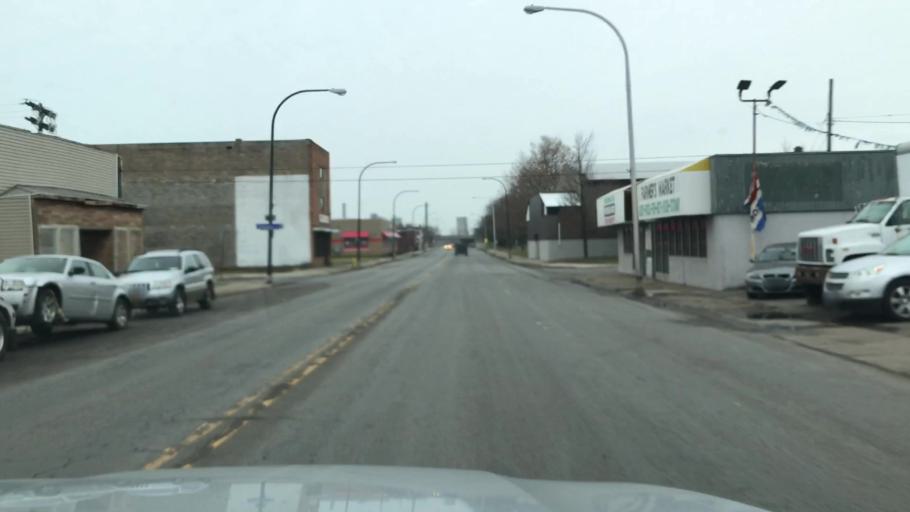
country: US
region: New York
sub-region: Erie County
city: Lackawanna
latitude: 42.8273
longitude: -78.8449
